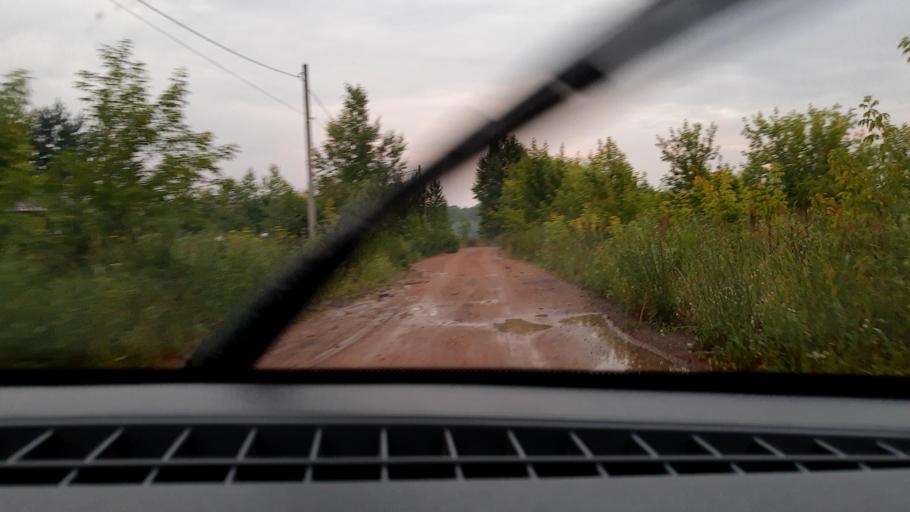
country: RU
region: Bashkortostan
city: Ufa
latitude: 54.7569
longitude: 55.9239
